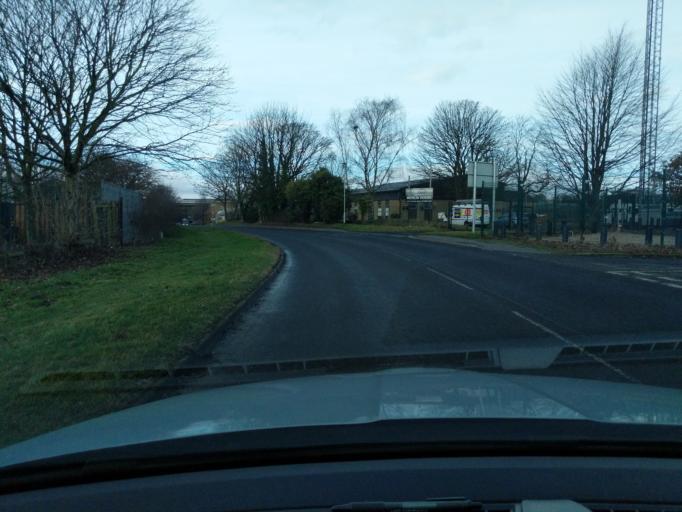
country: GB
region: England
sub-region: North Yorkshire
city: Catterick
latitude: 54.3941
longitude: -1.6553
